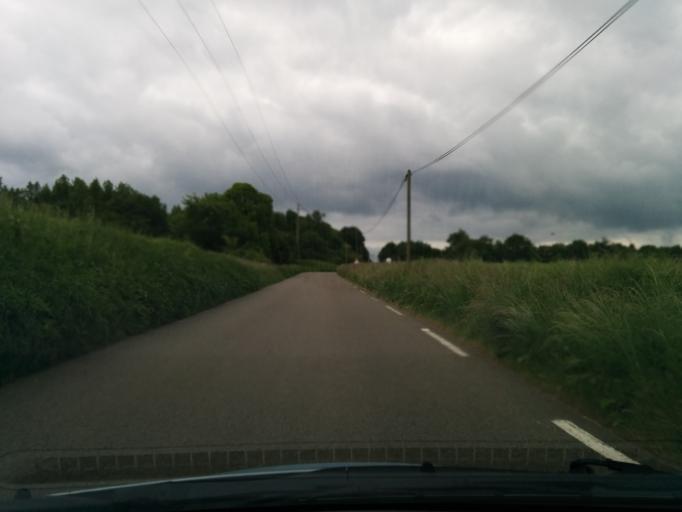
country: FR
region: Ile-de-France
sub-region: Departement des Yvelines
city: Issou
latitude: 49.0217
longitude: 1.8012
